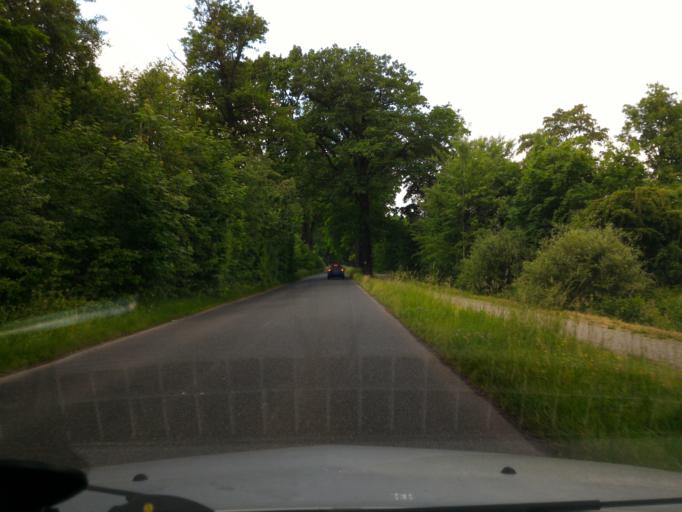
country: DE
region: Saxony
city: Zittau
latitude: 50.8811
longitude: 14.8213
